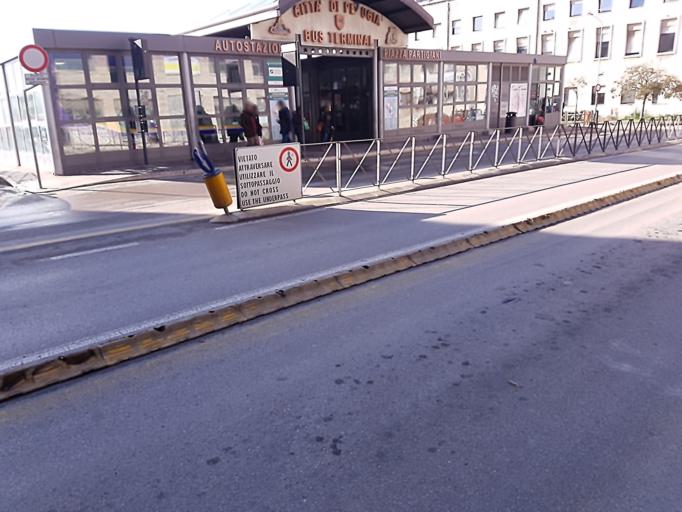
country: IT
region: Umbria
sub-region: Provincia di Perugia
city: Perugia
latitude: 43.1060
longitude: 12.3880
